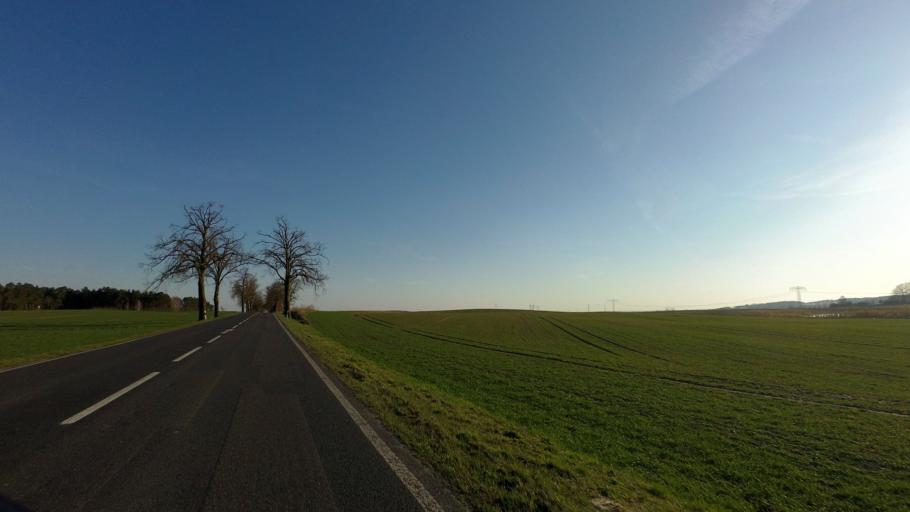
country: DE
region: Brandenburg
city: Britz
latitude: 52.9051
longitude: 13.8022
